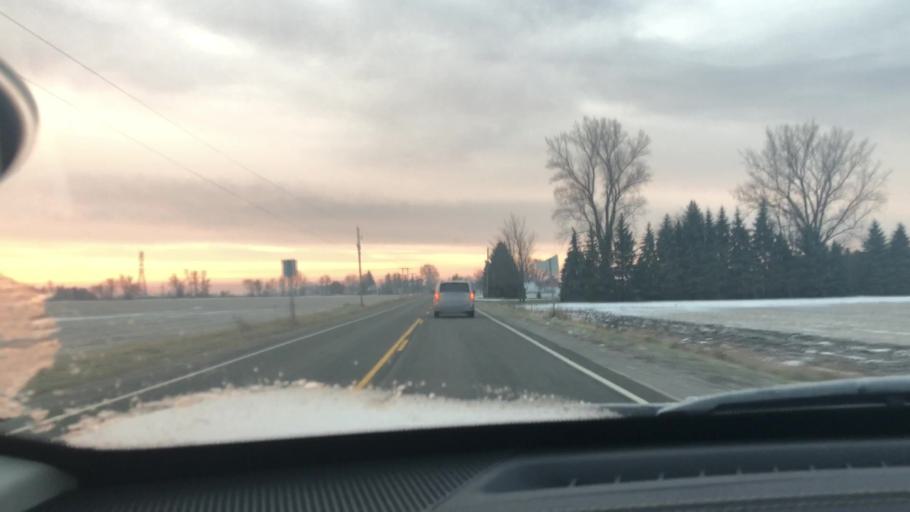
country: US
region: Michigan
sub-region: Saginaw County
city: Zilwaukee
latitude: 43.5056
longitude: -83.8362
